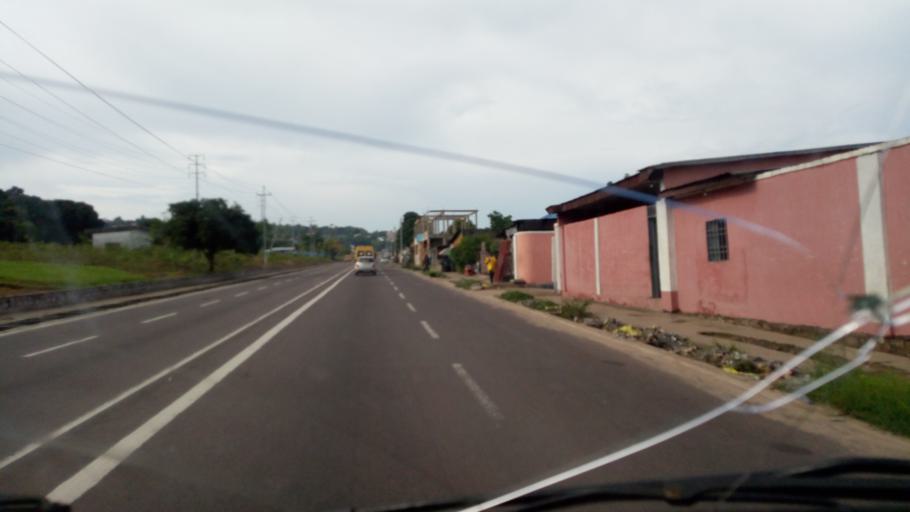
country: CD
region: Kinshasa
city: Kinshasa
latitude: -4.4306
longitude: 15.2579
